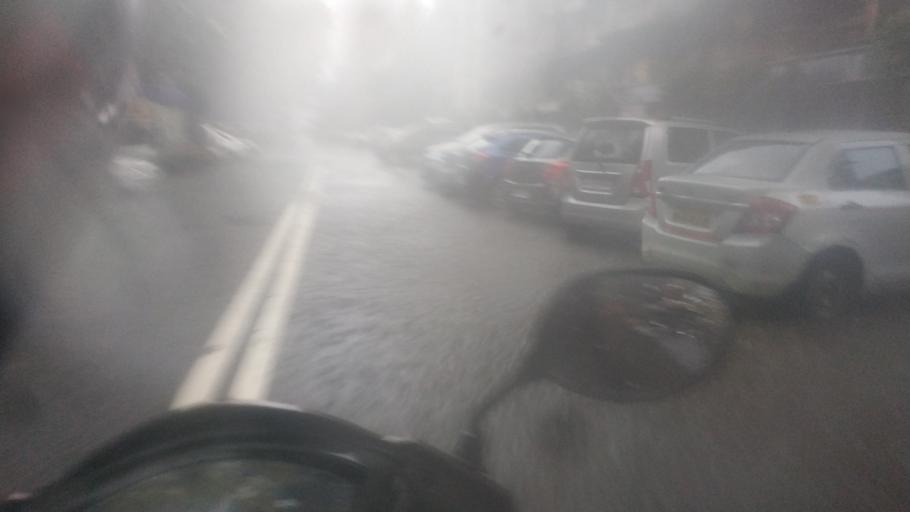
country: IN
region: Maharashtra
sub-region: Mumbai Suburban
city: Mumbai
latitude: 19.1151
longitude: 72.8369
